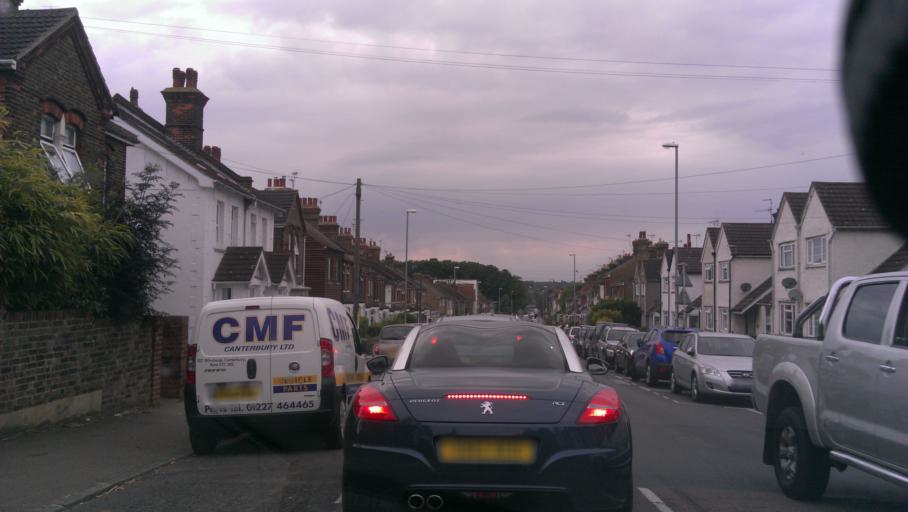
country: GB
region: England
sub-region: Kent
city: Faversham
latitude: 51.3126
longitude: 0.9053
